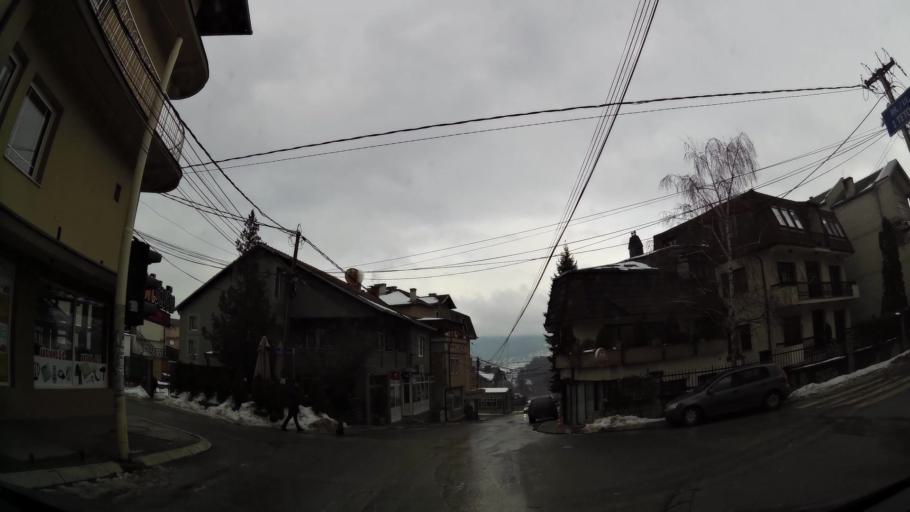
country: XK
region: Pristina
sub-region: Komuna e Prishtines
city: Pristina
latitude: 42.6616
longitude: 21.1748
